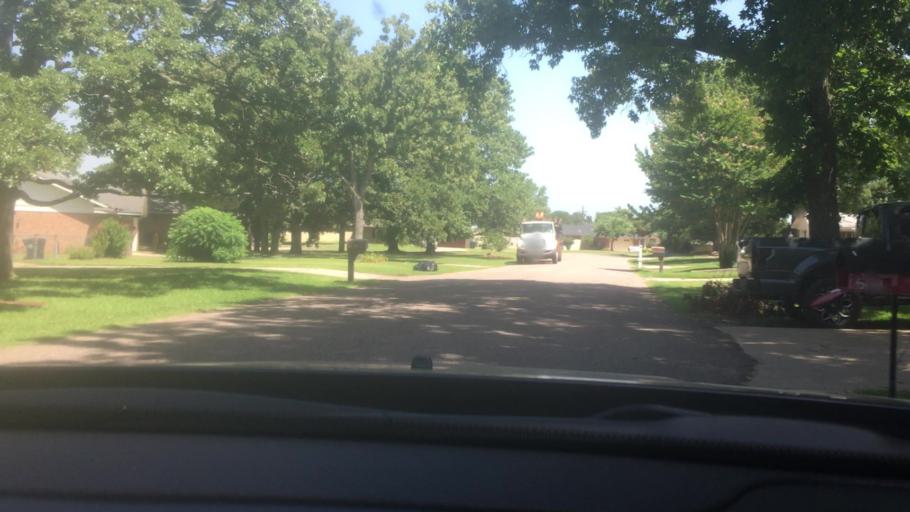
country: US
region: Oklahoma
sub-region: Pontotoc County
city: Ada
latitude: 34.7796
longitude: -96.6381
